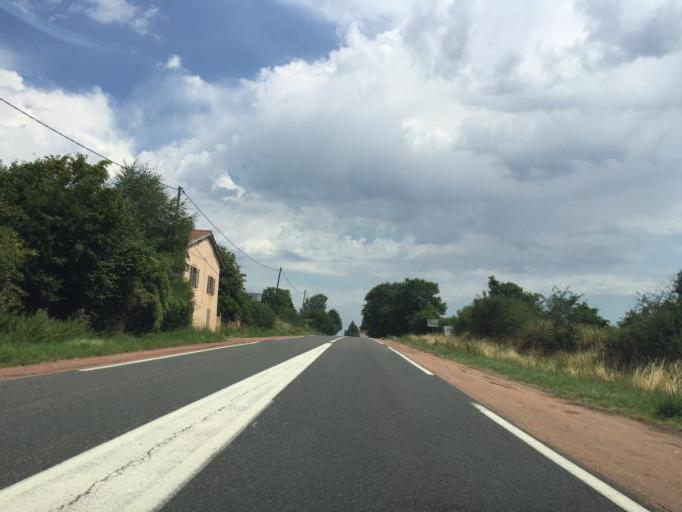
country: FR
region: Rhone-Alpes
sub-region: Departement du Rhone
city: Bully
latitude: 45.8576
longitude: 4.5663
